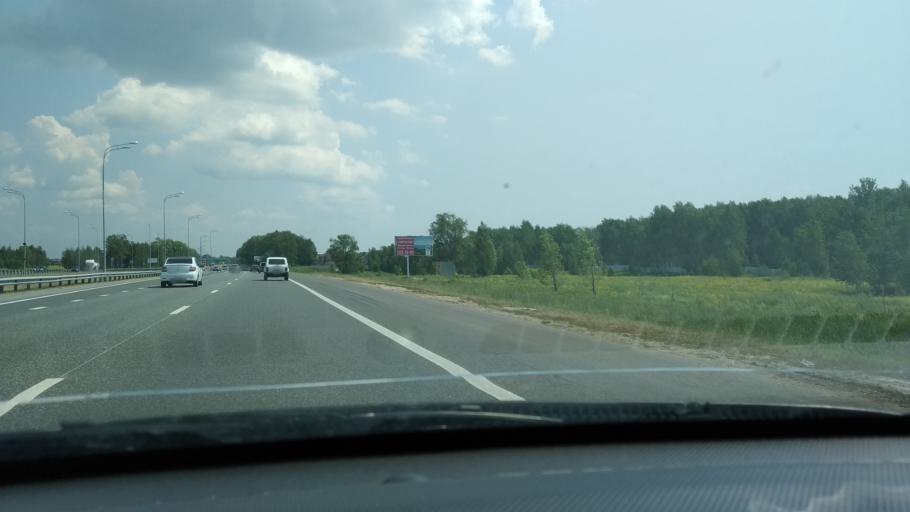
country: RU
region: Tatarstan
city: Osinovo
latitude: 55.8639
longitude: 48.7843
